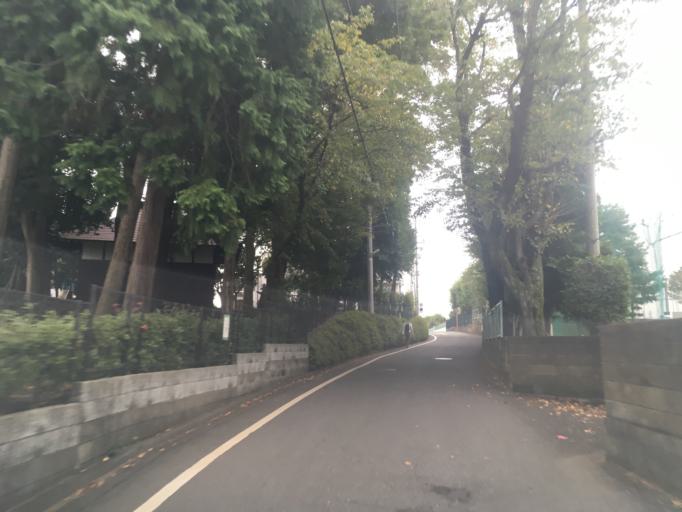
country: JP
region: Tokyo
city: Higashimurayama-shi
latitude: 35.7587
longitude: 139.4598
